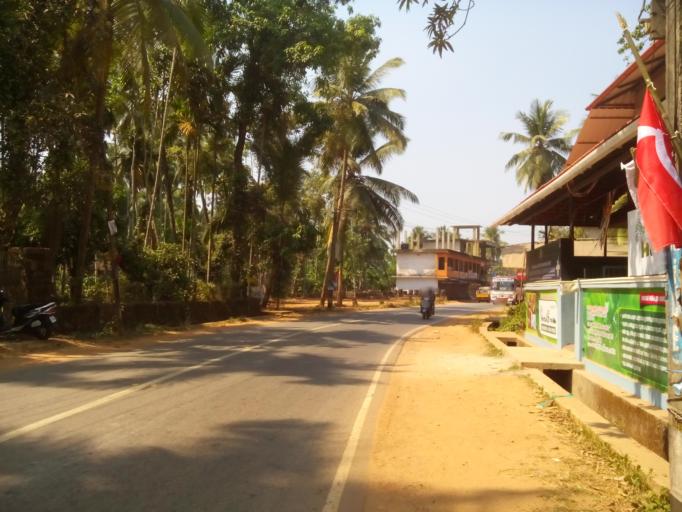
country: IN
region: Kerala
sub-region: Kozhikode
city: Nadapuram
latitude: 11.6879
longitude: 75.6720
